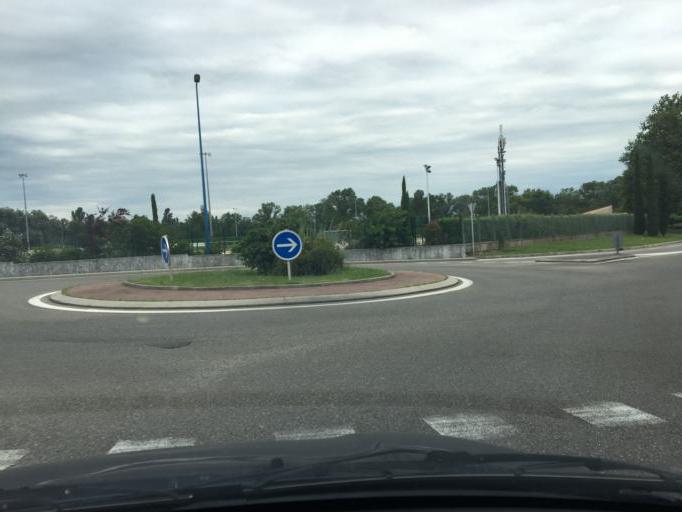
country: FR
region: Rhone-Alpes
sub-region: Departement de l'Ardeche
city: Guilherand-Granges
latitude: 44.9361
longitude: 4.8822
